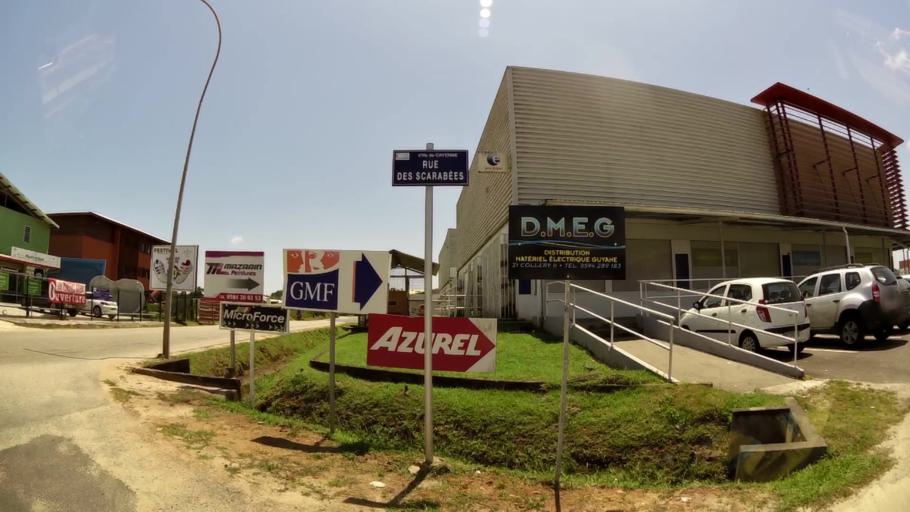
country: GF
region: Guyane
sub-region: Guyane
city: Cayenne
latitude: 4.8998
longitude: -52.3284
